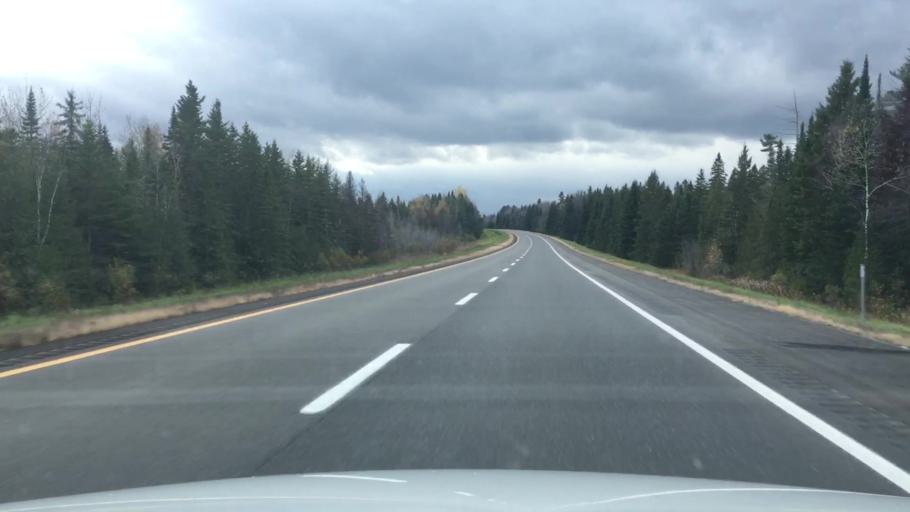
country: US
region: Maine
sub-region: Penobscot County
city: Patten
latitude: 46.0932
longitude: -68.1973
